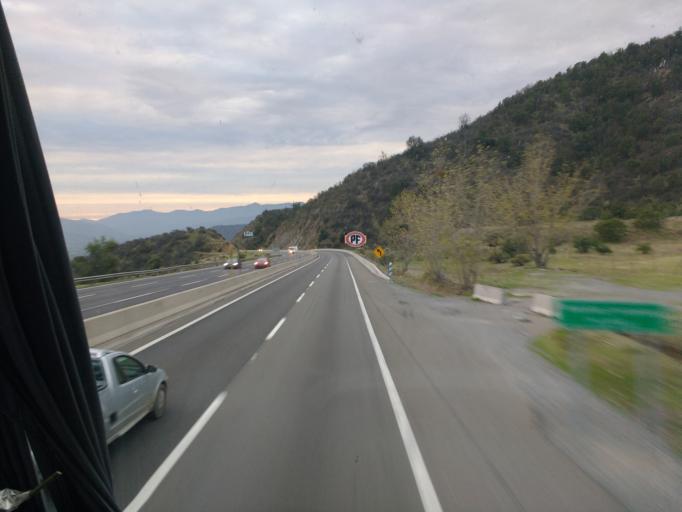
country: CL
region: Santiago Metropolitan
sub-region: Provincia de Talagante
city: Penaflor
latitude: -33.4560
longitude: -70.9695
